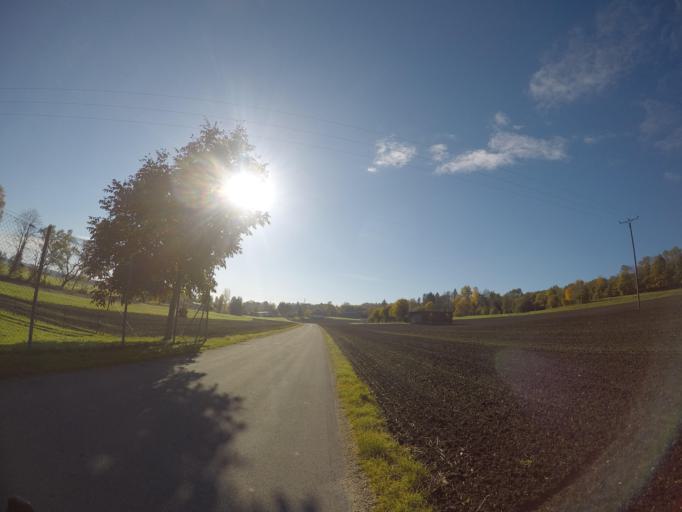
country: DE
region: Baden-Wuerttemberg
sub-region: Tuebingen Region
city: Saulgau
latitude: 48.0363
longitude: 9.4743
